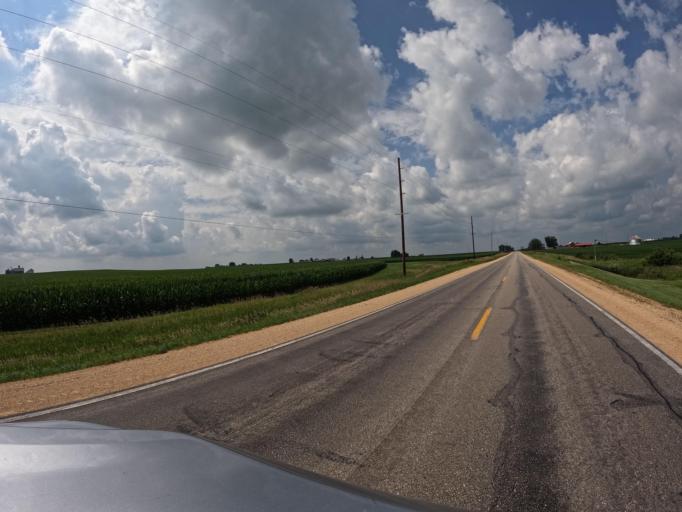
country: US
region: Iowa
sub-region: Clinton County
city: Camanche
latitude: 41.7733
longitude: -90.3548
